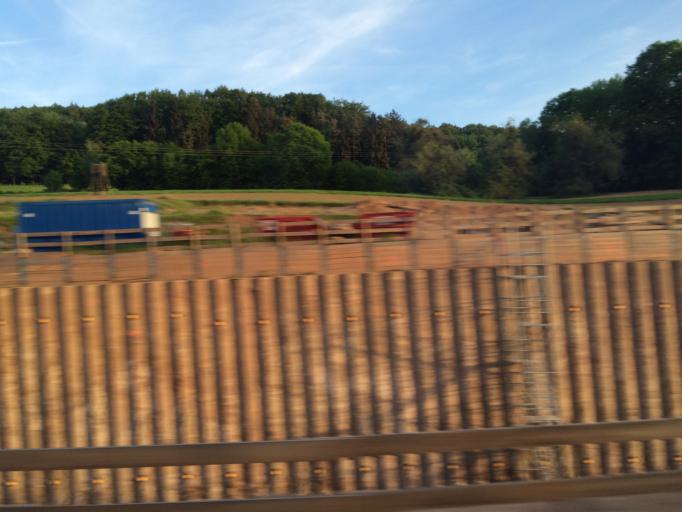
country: DE
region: Bavaria
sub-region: Regierungsbezirk Unterfranken
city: Laufach
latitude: 50.0105
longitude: 9.3096
